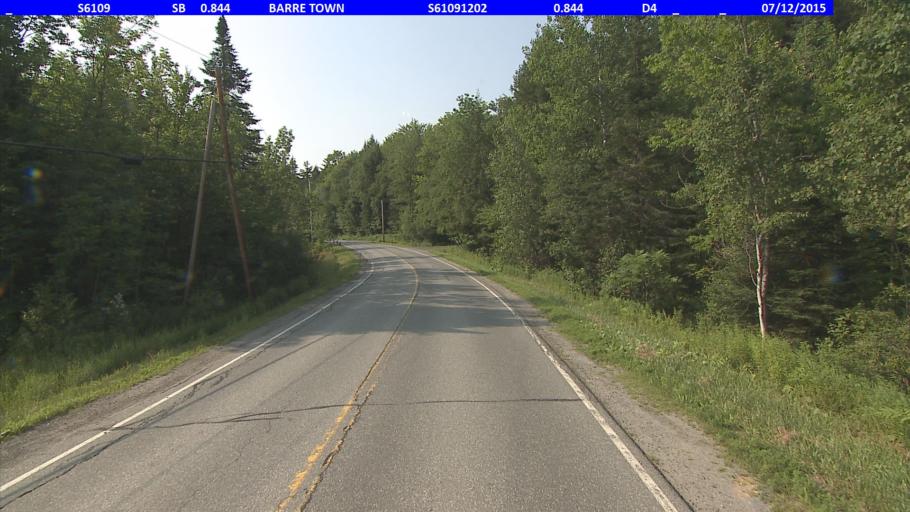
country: US
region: Vermont
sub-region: Washington County
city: South Barre
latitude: 44.1665
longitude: -72.4927
